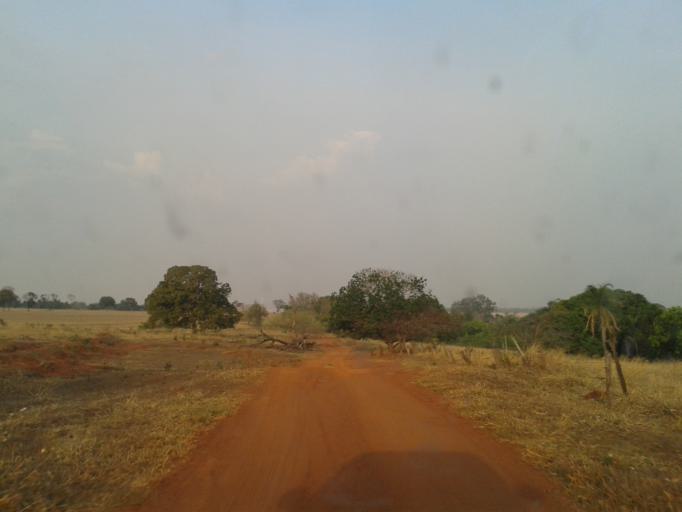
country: BR
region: Minas Gerais
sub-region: Capinopolis
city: Capinopolis
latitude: -18.8080
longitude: -49.7343
